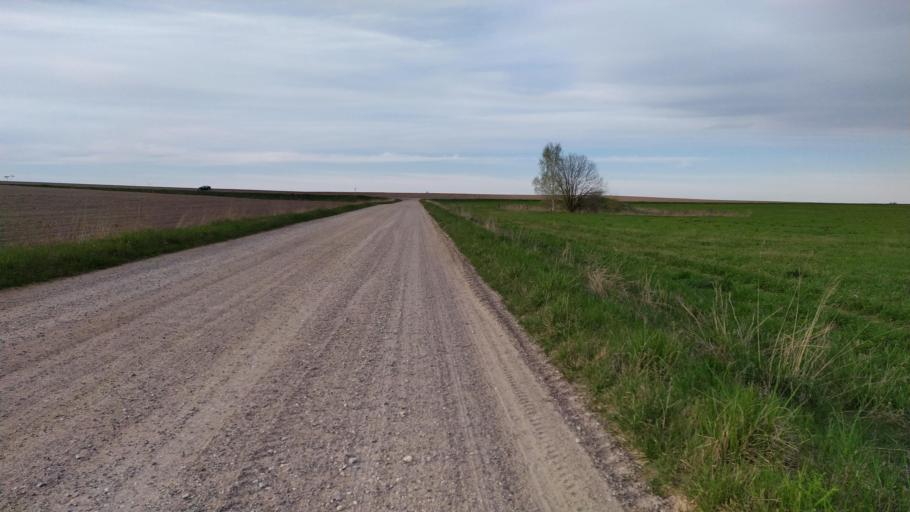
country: BY
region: Brest
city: Kamyanyets
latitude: 52.4157
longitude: 23.6756
